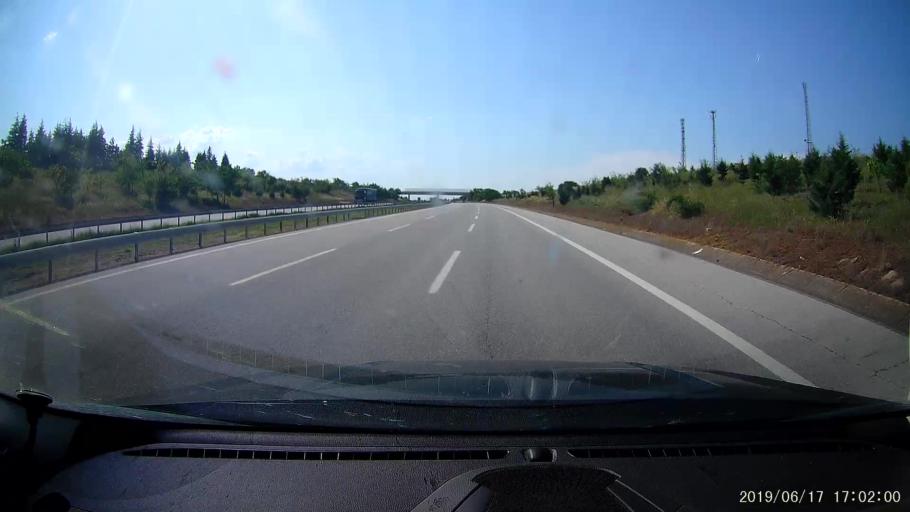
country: TR
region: Edirne
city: Haskoy
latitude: 41.6350
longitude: 26.7914
